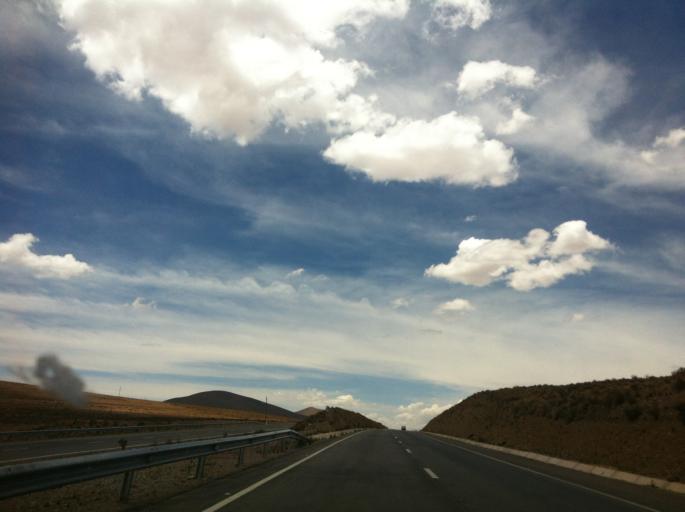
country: BO
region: La Paz
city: Eucaliptus
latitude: -17.5410
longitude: -67.3902
